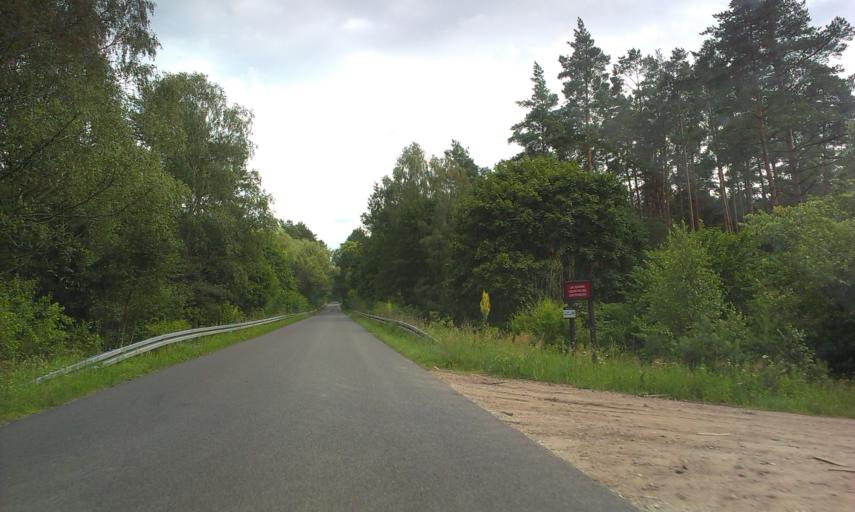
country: PL
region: Greater Poland Voivodeship
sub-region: Powiat zlotowski
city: Zlotow
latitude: 53.4922
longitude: 16.9852
